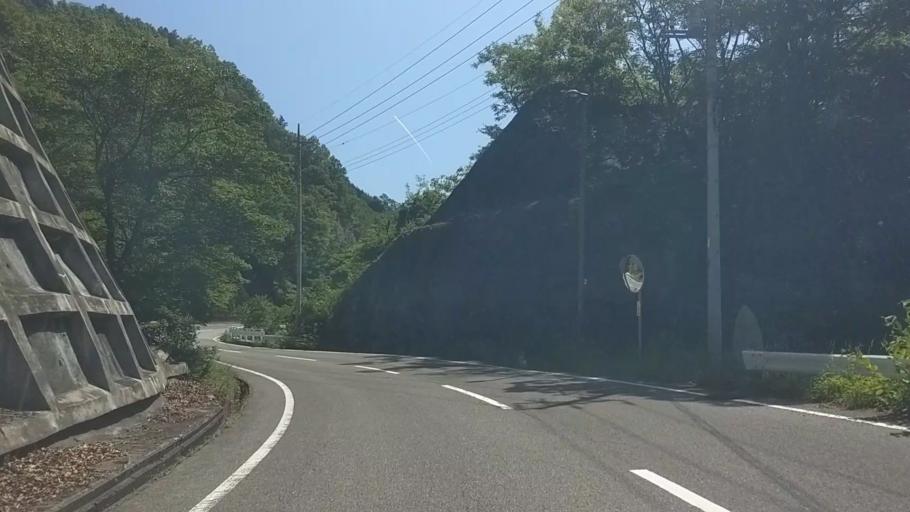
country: JP
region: Yamanashi
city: Ryuo
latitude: 35.5116
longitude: 138.4431
